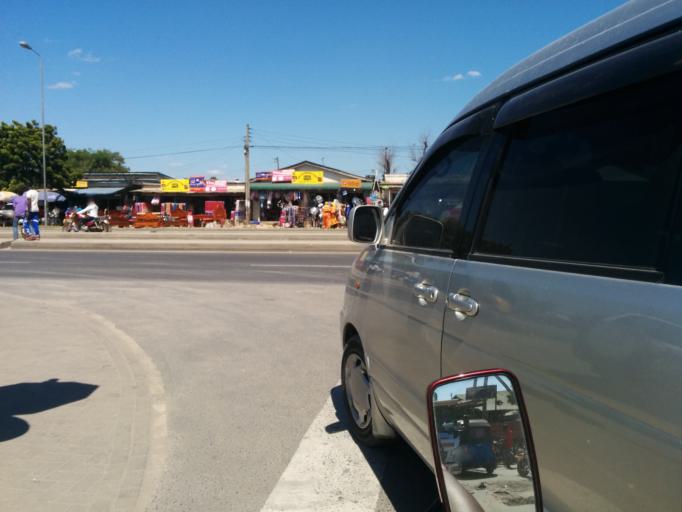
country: TZ
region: Dar es Salaam
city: Magomeni
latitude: -6.7987
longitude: 39.2332
